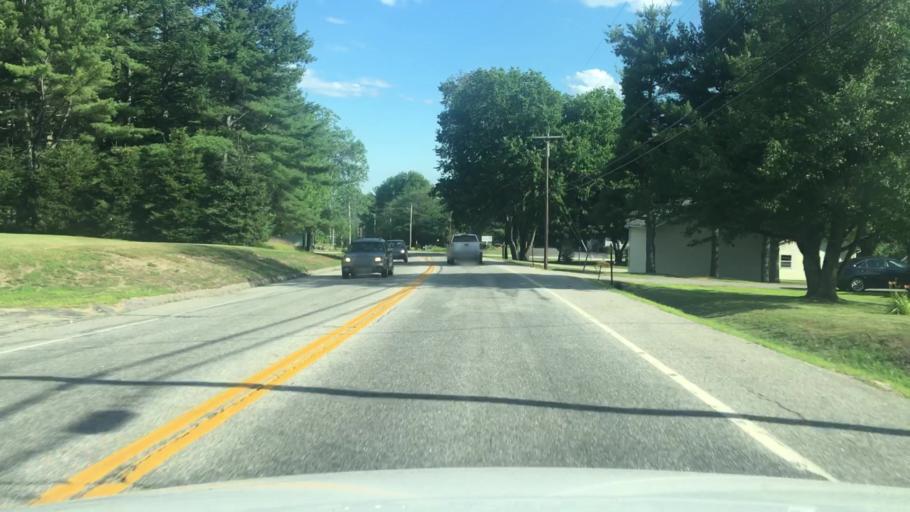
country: US
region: Maine
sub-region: Franklin County
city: Jay
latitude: 44.5144
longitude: -70.2228
